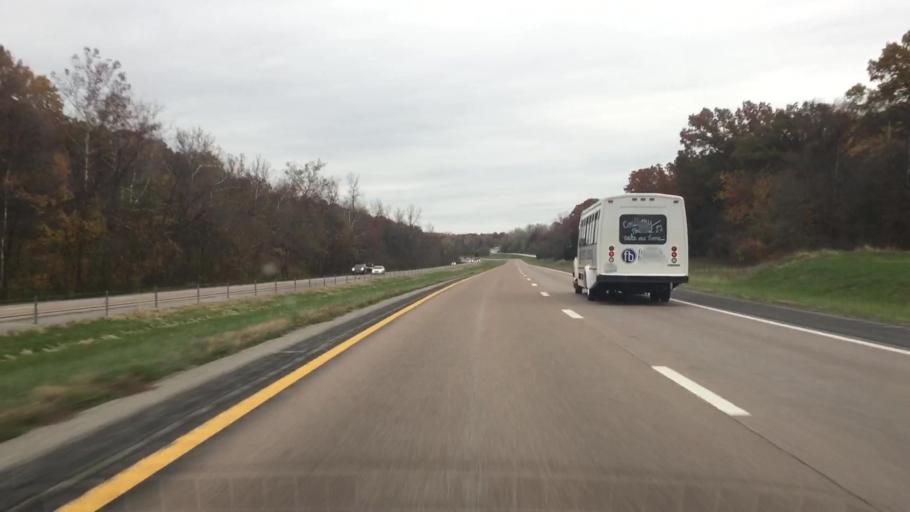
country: US
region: Missouri
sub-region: Cole County
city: Jefferson City
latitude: 38.6614
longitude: -92.2245
